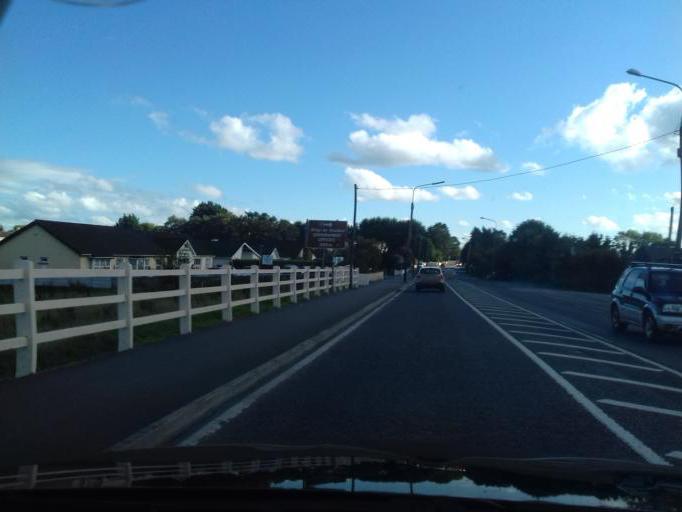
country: IE
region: Leinster
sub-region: Uibh Fhaili
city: Tullamore
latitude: 53.2638
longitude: -7.4853
